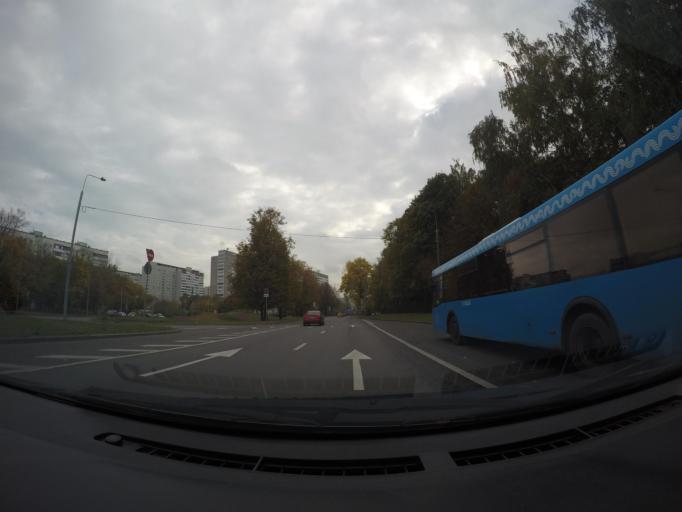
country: RU
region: Moscow
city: Ivanovskoye
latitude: 55.7686
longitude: 37.8214
